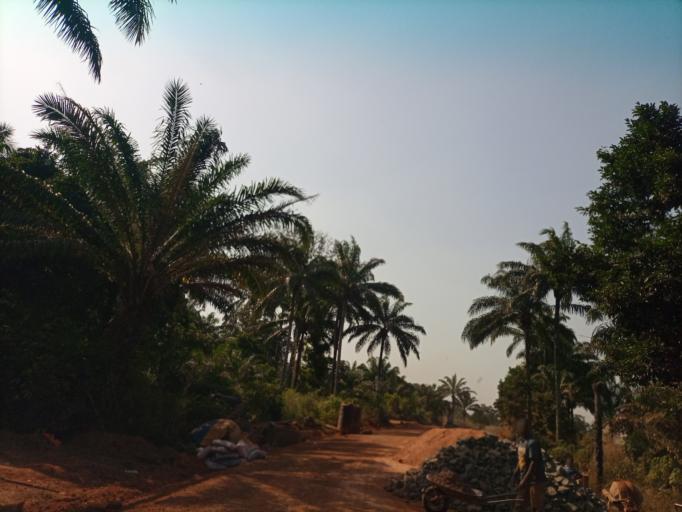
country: NG
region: Enugu
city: Aku
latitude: 6.7023
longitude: 7.3165
